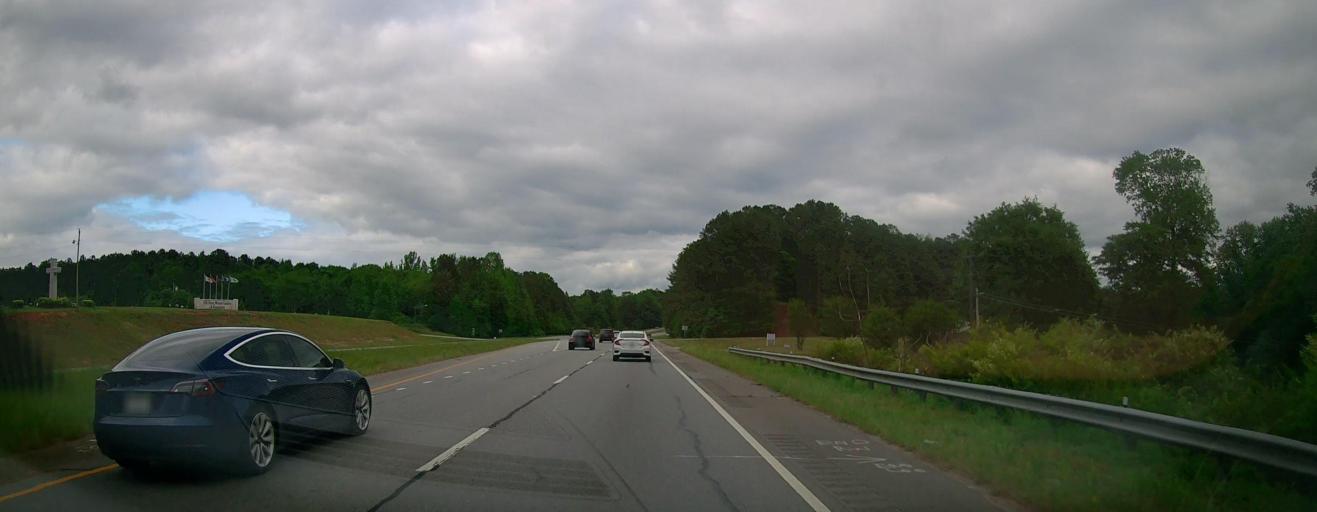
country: US
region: Georgia
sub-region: Walton County
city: Monroe
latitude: 33.8187
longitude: -83.6734
